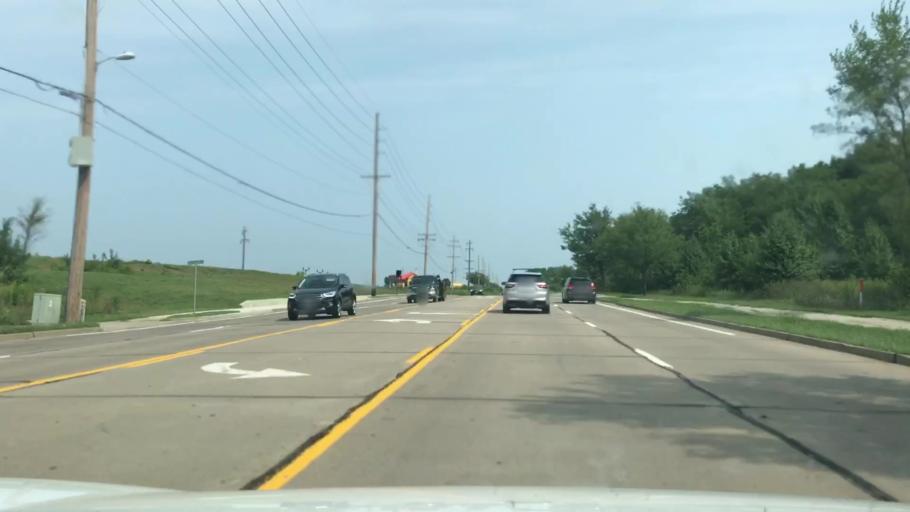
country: US
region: Missouri
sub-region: Saint Charles County
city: Dardenne Prairie
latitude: 38.7964
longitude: -90.7360
